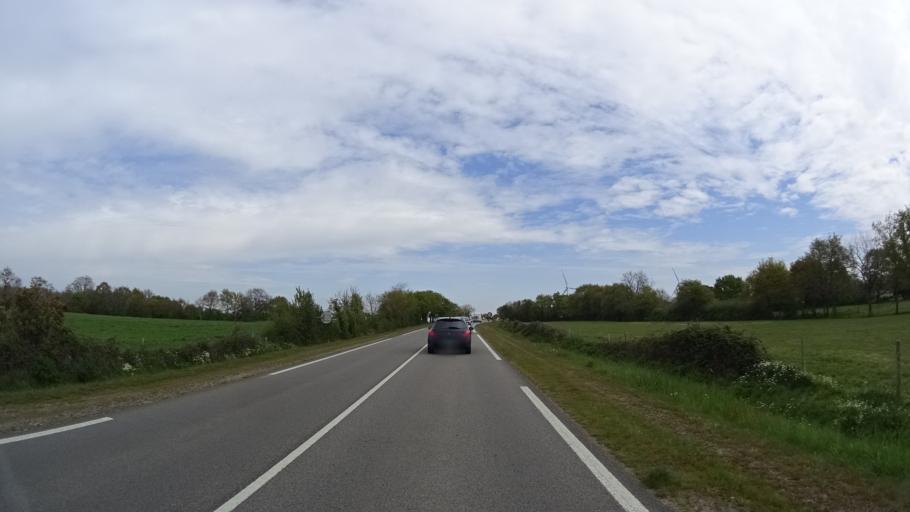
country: FR
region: Pays de la Loire
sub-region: Departement de la Loire-Atlantique
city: Saint-Hilaire-de-Chaleons
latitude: 47.0726
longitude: -1.8959
